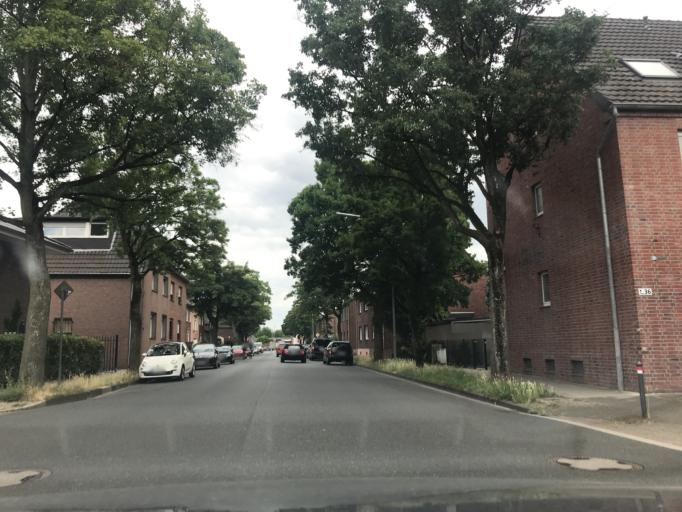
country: DE
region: North Rhine-Westphalia
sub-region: Regierungsbezirk Dusseldorf
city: Neuss
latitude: 51.1618
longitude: 6.6722
